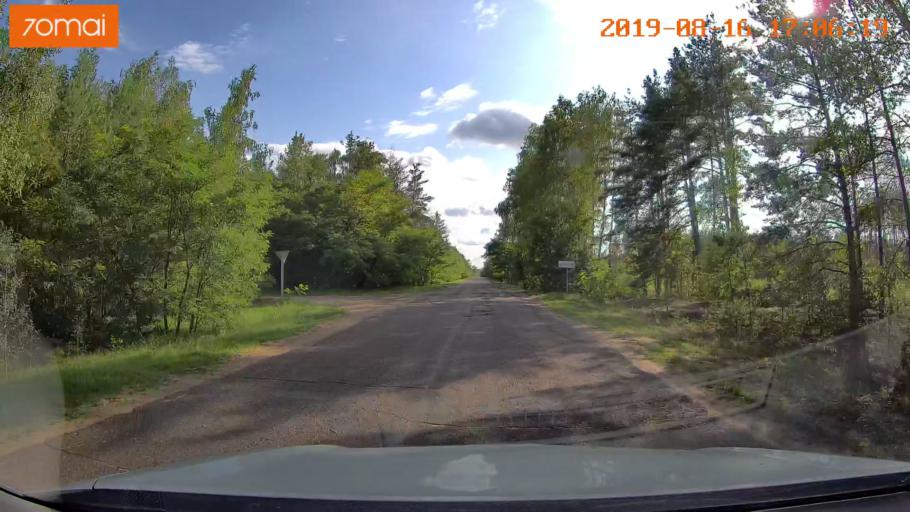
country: BY
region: Mogilev
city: Hlusha
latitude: 53.2283
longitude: 28.9345
